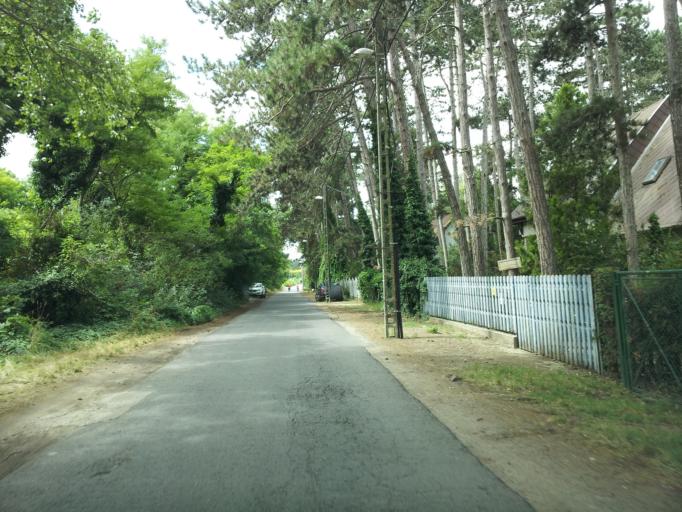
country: HU
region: Somogy
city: Balatonszabadi
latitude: 46.9418
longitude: 18.1324
